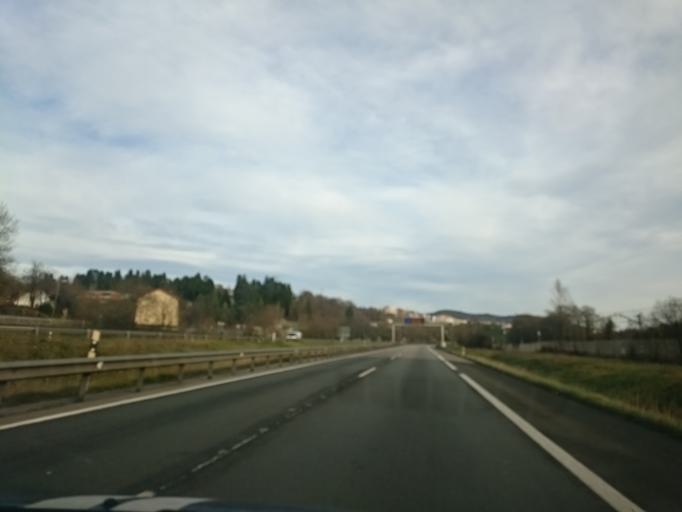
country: ES
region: Asturias
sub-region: Province of Asturias
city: Oviedo
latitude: 43.3355
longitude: -5.8699
